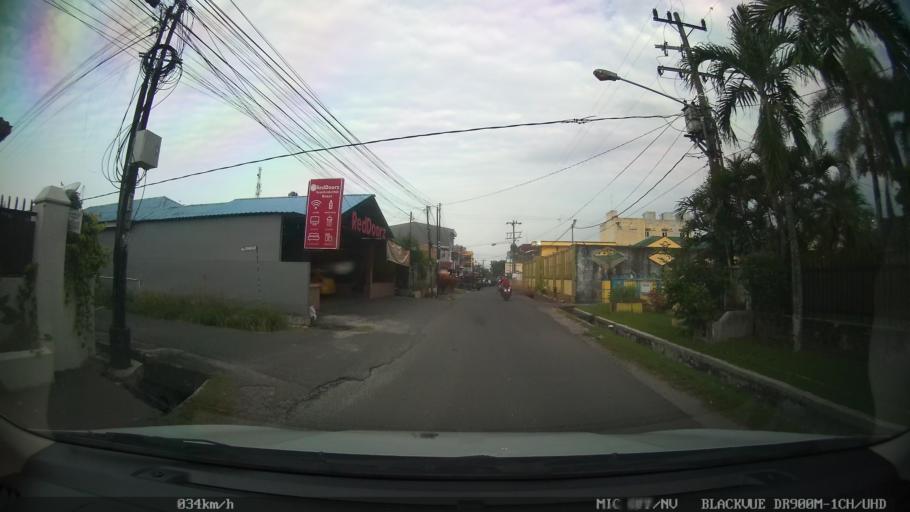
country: ID
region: North Sumatra
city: Sunggal
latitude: 3.5550
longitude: 98.6311
